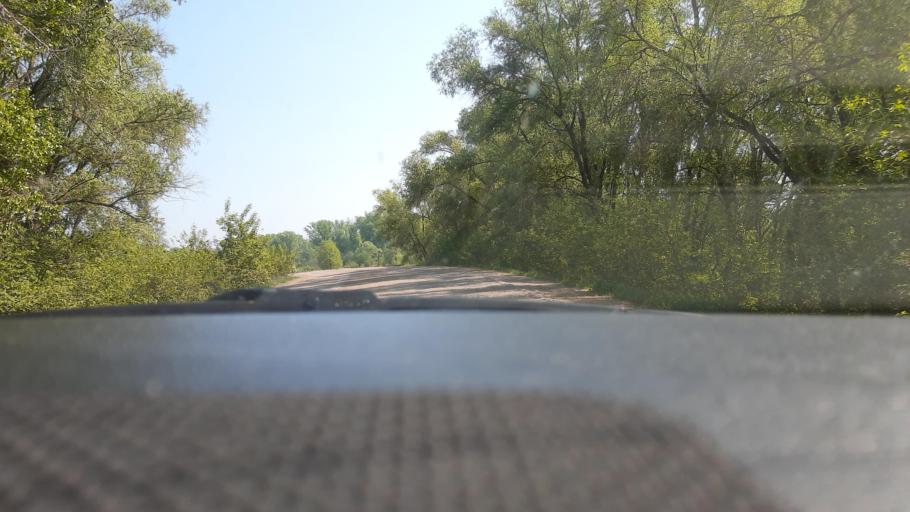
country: RU
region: Bashkortostan
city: Chishmy
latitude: 54.4432
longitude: 55.2760
